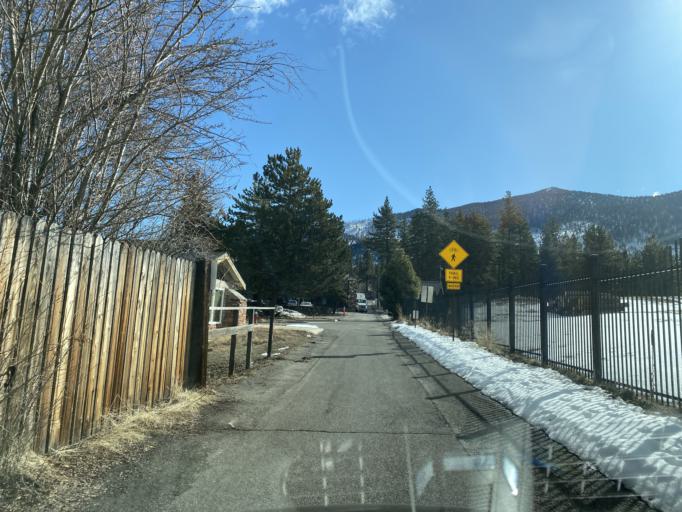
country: US
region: Nevada
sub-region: Douglas County
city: Kingsbury
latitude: 38.9691
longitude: -119.9381
